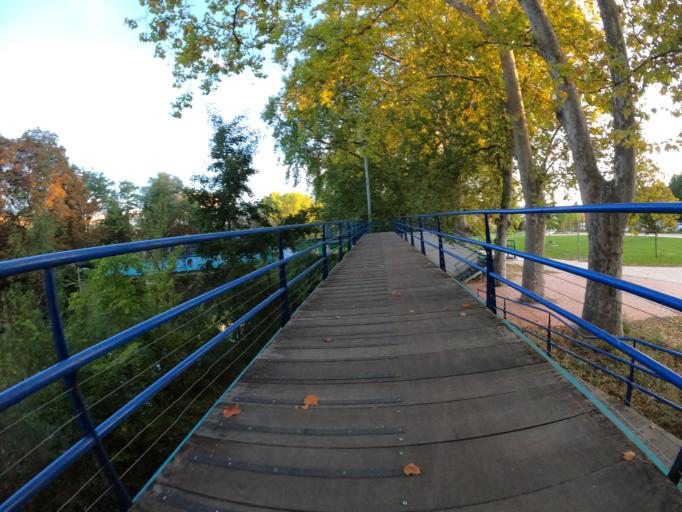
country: ES
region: Navarre
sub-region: Provincia de Navarra
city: Ermitagana
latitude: 42.8211
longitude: -1.6608
